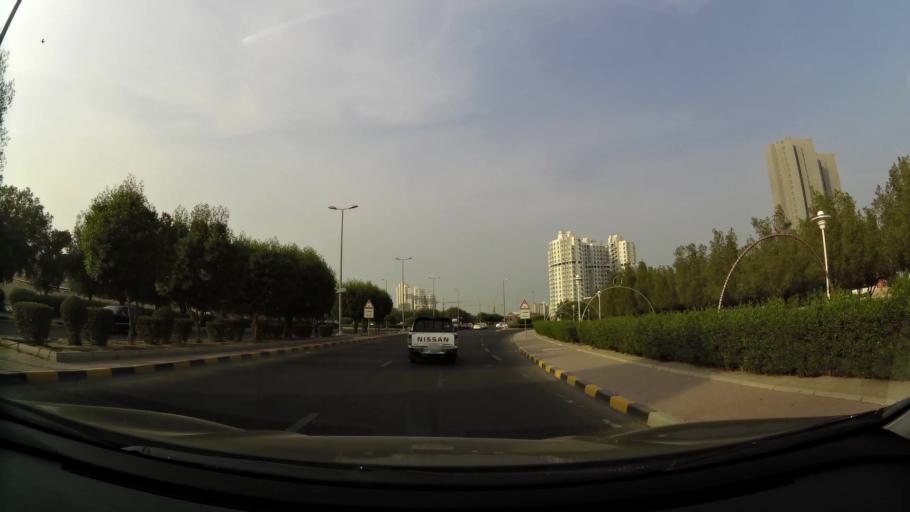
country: KW
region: Mubarak al Kabir
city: Sabah as Salim
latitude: 29.2557
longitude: 48.0783
